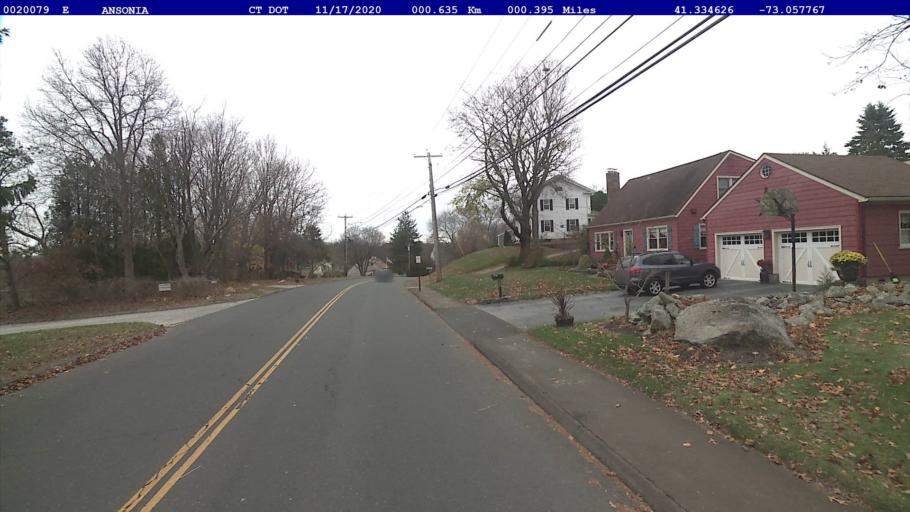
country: US
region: Connecticut
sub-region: New Haven County
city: Ansonia
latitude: 41.3346
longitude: -73.0577
